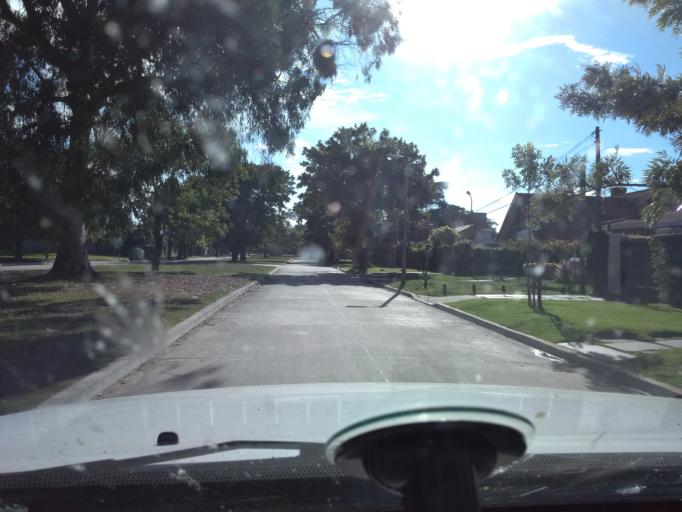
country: UY
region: Canelones
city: Paso de Carrasco
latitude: -34.8867
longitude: -56.0641
